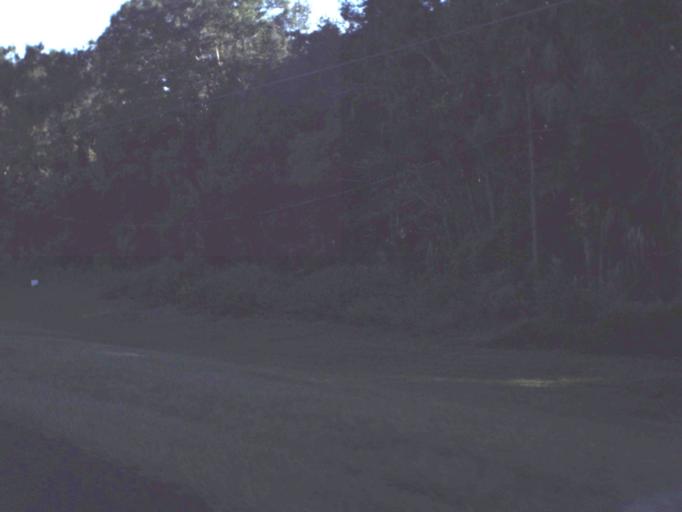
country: US
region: Florida
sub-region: Citrus County
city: Crystal River
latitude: 28.9232
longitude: -82.6123
